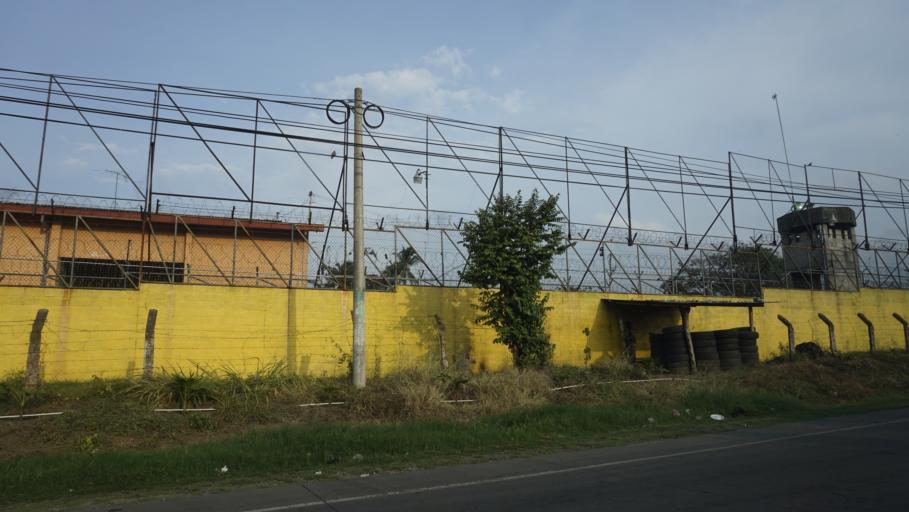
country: SV
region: Santa Ana
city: Santa Ana
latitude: 14.0029
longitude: -89.5492
